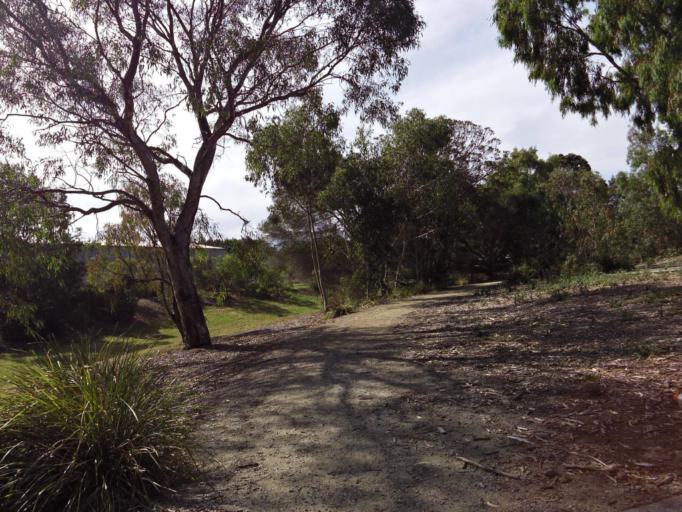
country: AU
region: Victoria
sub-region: Casey
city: Eumemmerring
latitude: -37.9953
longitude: 145.2452
